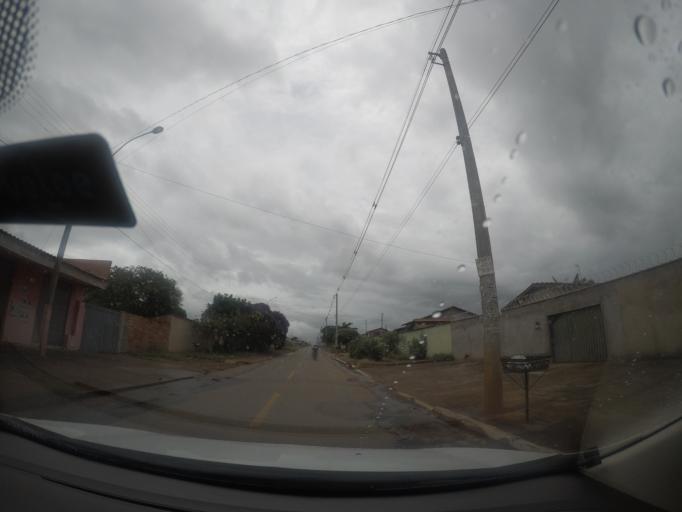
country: BR
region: Goias
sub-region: Trindade
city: Trindade
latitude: -16.6405
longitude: -49.3878
